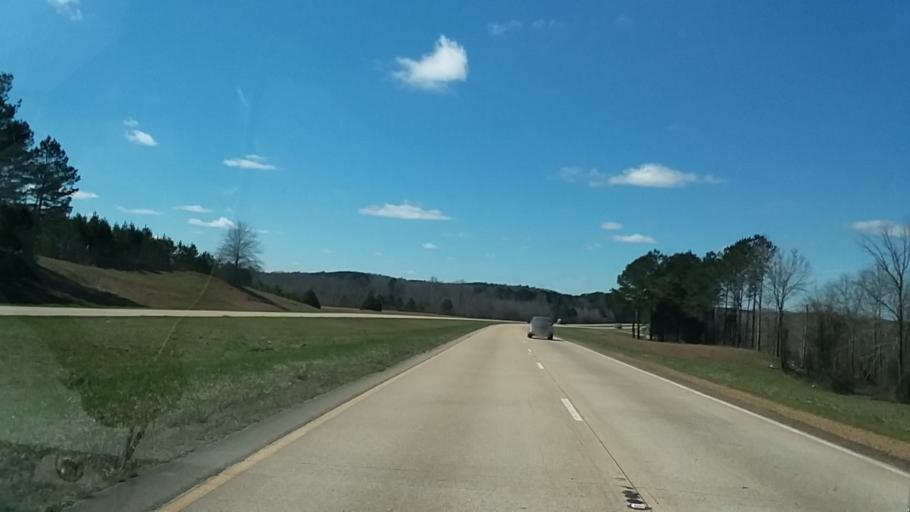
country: US
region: Mississippi
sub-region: Tishomingo County
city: Iuka
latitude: 34.8084
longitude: -88.2715
